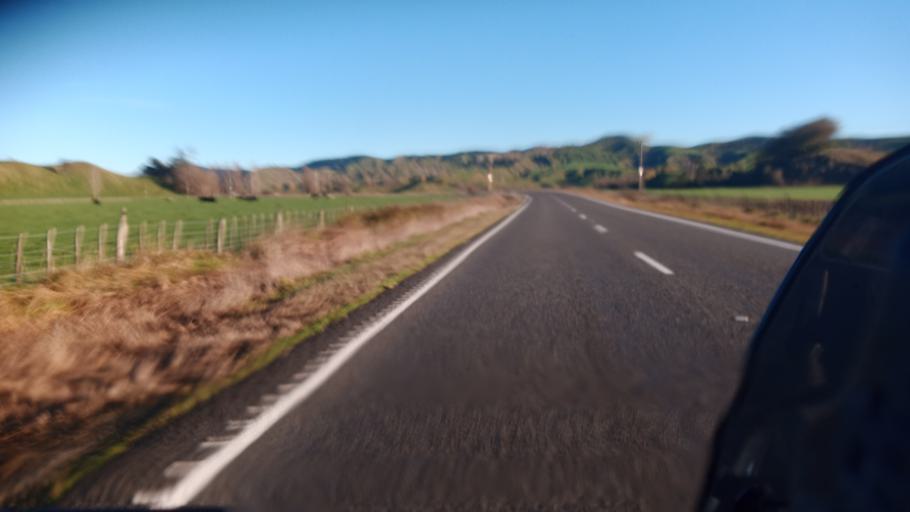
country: NZ
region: Hawke's Bay
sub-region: Wairoa District
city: Wairoa
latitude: -39.0183
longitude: 177.3713
